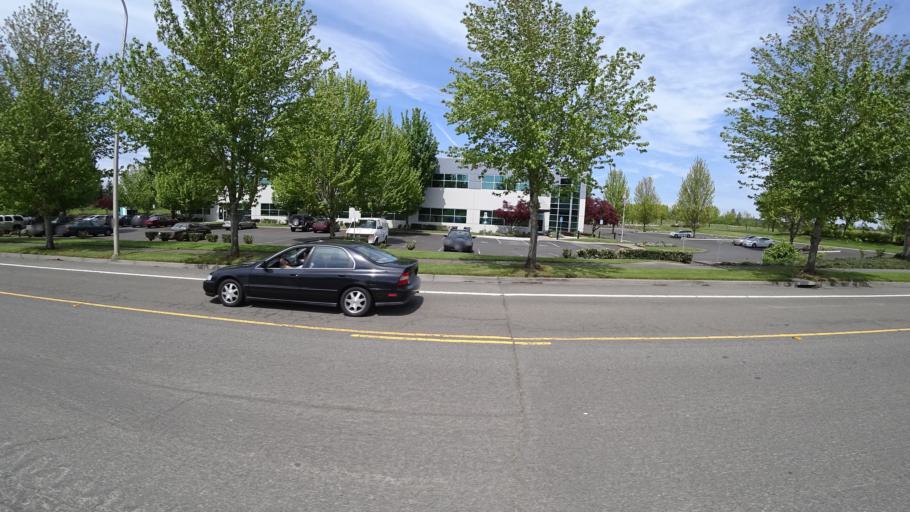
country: US
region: Oregon
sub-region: Washington County
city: Rockcreek
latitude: 45.5654
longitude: -122.9067
